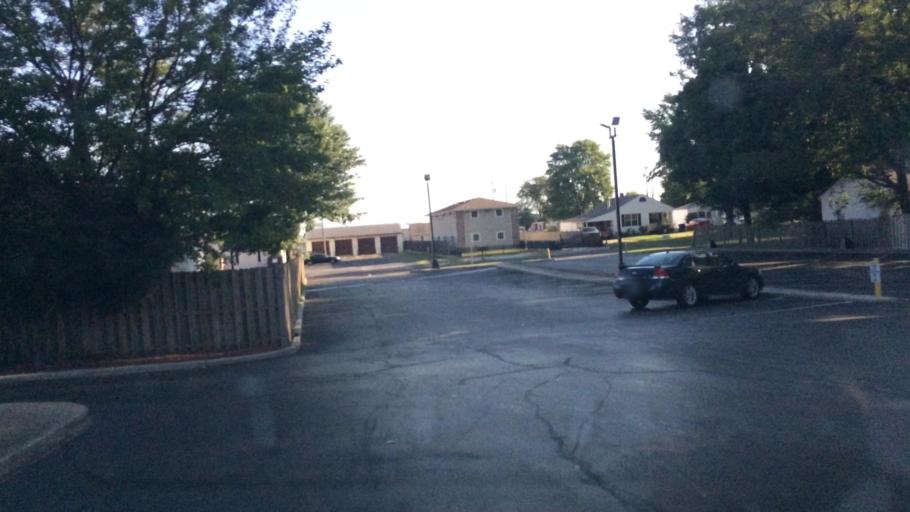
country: US
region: Missouri
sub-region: Greene County
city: Springfield
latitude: 37.2043
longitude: -93.2614
